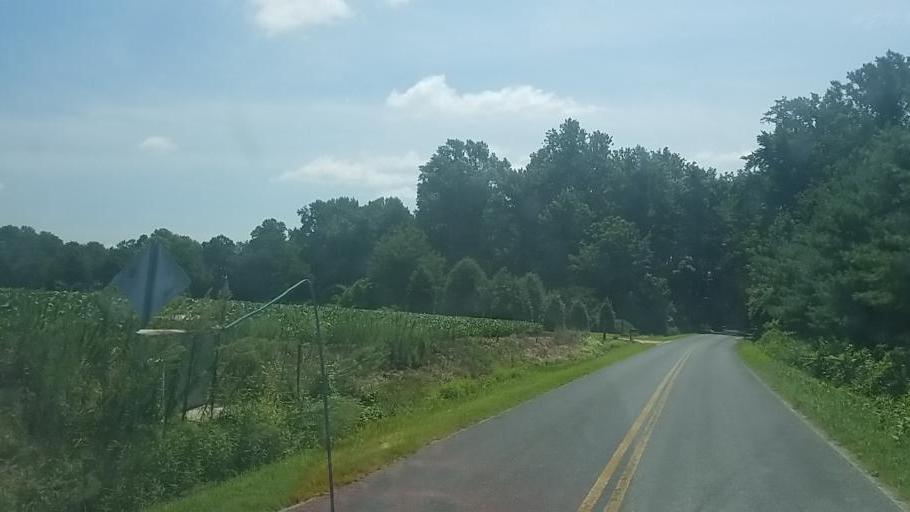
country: US
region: Maryland
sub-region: Caroline County
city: Ridgely
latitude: 38.9110
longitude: -75.9362
